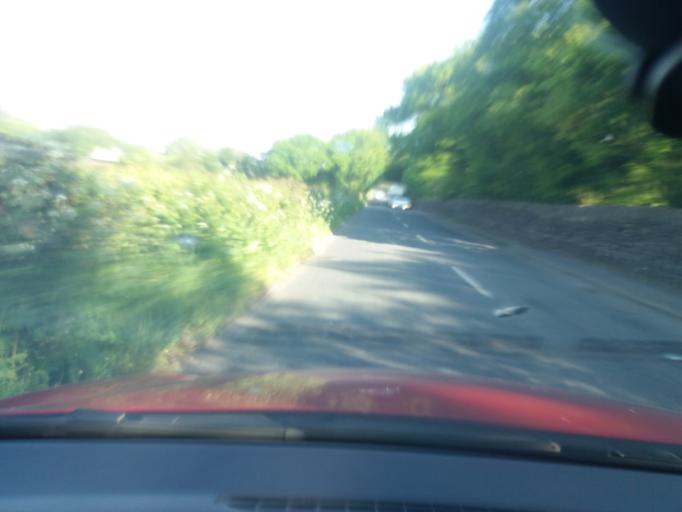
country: GB
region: England
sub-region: Borough of Wigan
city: Haigh
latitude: 53.6200
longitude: -2.5819
